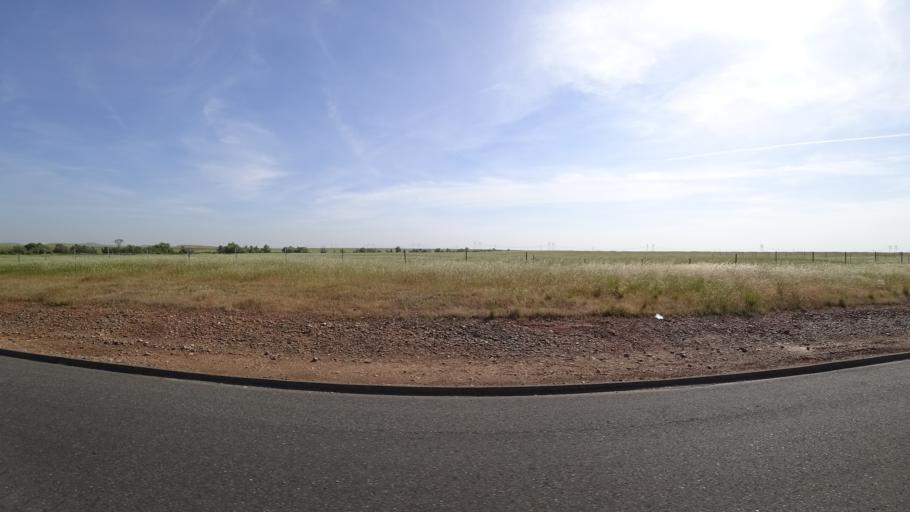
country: US
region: California
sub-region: Butte County
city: Thermalito
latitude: 39.5941
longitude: -121.6467
